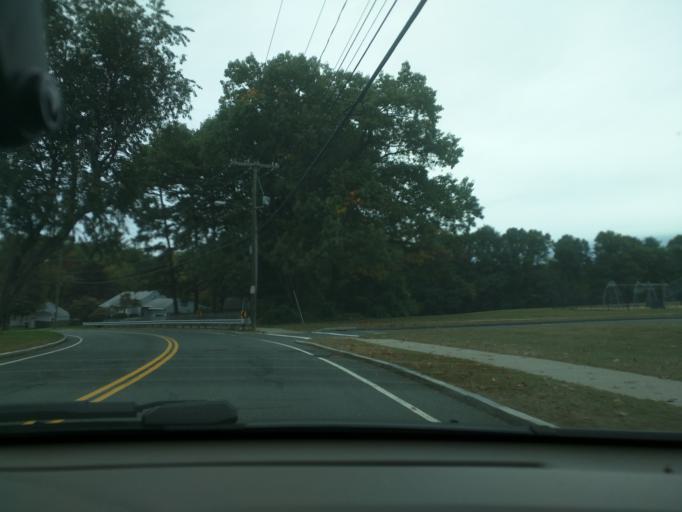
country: US
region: Massachusetts
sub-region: Hampden County
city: East Longmeadow
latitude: 42.0736
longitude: -72.5453
